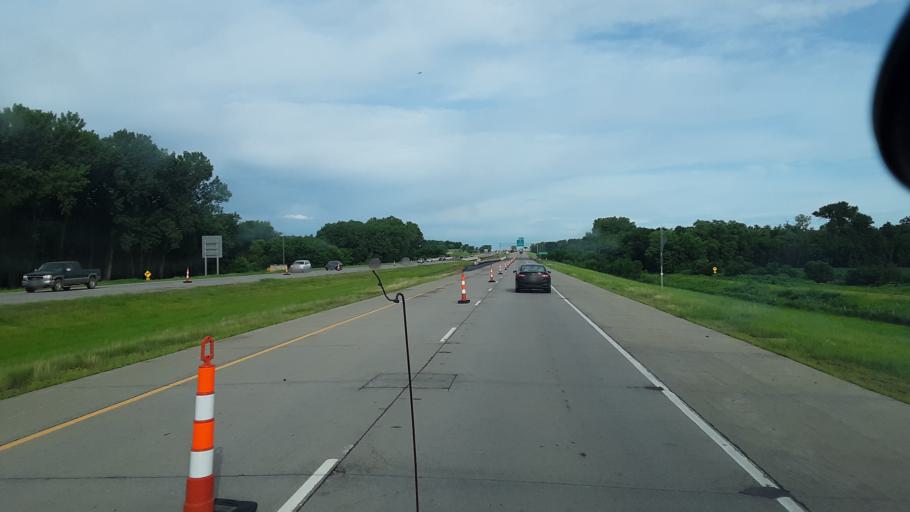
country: US
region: South Dakota
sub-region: Minnehaha County
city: Sioux Falls
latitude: 43.6096
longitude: -96.7406
